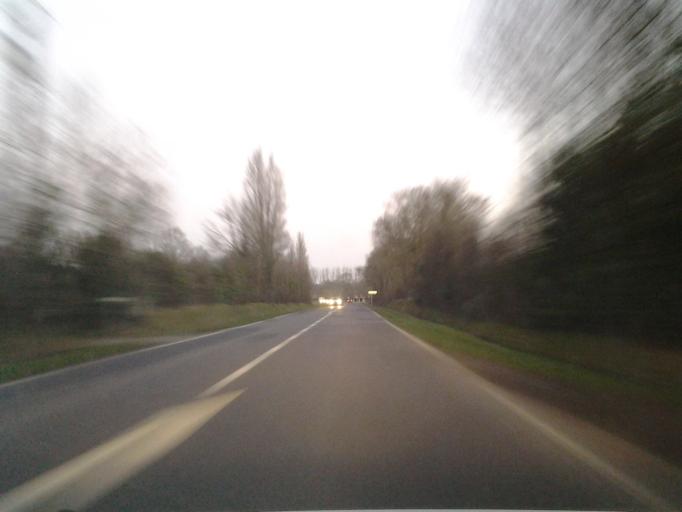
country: FR
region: Pays de la Loire
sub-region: Departement de la Vendee
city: Saint-Gervais
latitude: 46.8898
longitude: -1.9764
